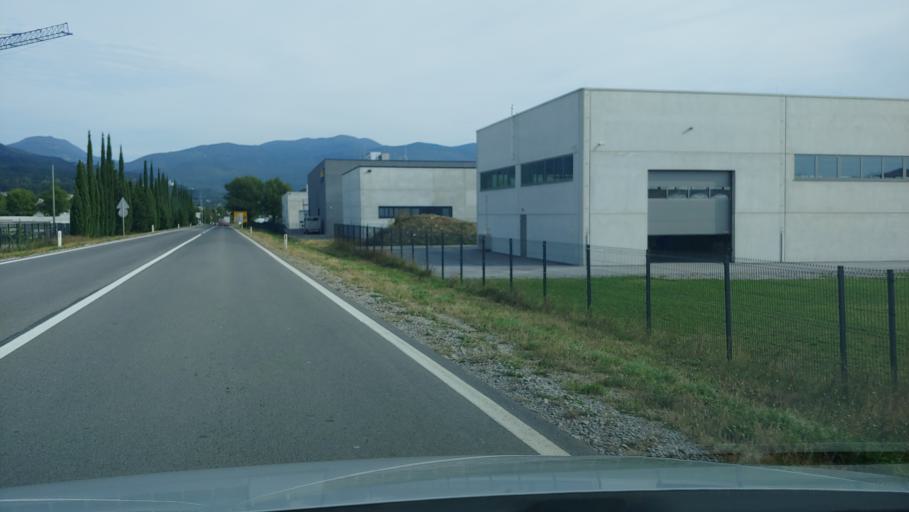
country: SI
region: Ajdovscina
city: Ajdovscina
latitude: 45.8825
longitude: 13.8968
